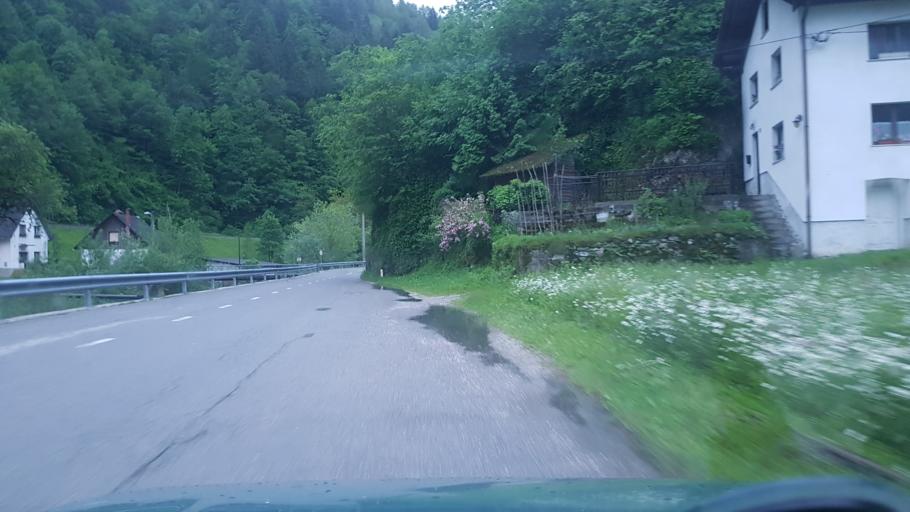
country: SI
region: Cerkno
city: Cerkno
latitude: 46.1780
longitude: 13.9187
